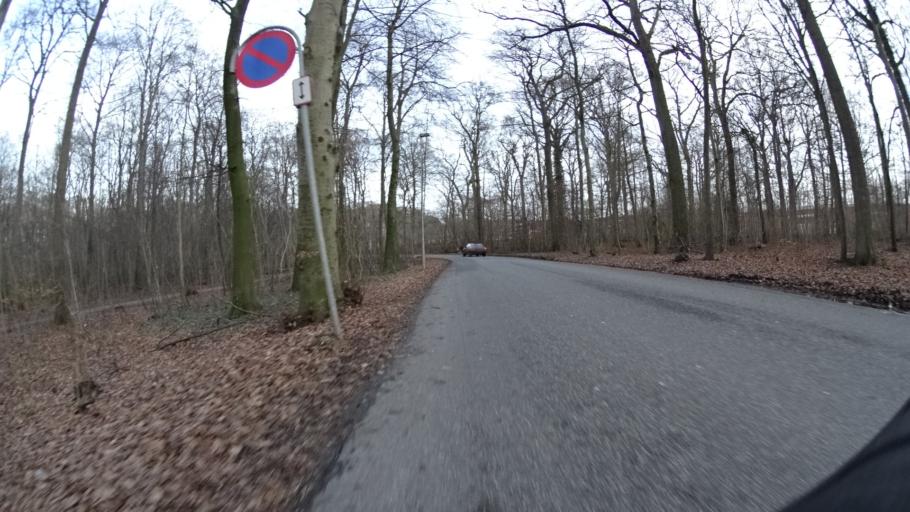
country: DK
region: Central Jutland
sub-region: Arhus Kommune
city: Arhus
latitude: 56.1222
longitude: 10.1833
